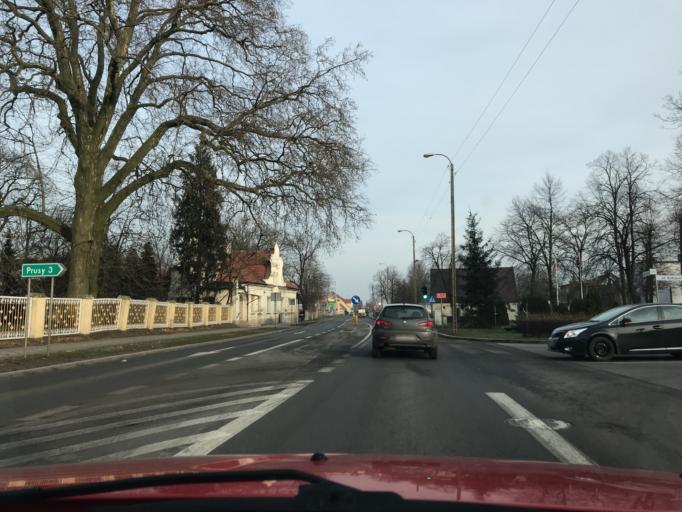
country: PL
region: Greater Poland Voivodeship
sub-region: Powiat jarocinski
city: Witaszyce
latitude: 51.9420
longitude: 17.5616
